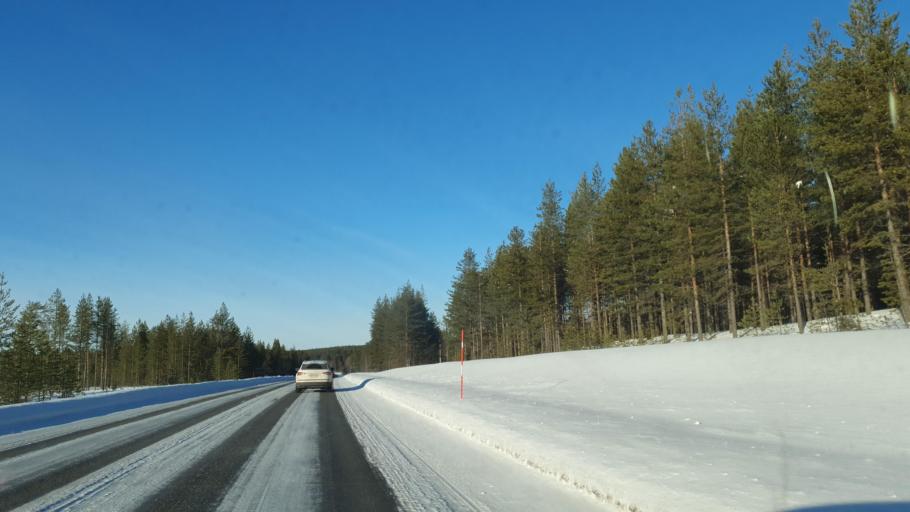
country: FI
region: Lapland
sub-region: Torniolaakso
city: Pello
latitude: 66.9312
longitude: 24.0827
